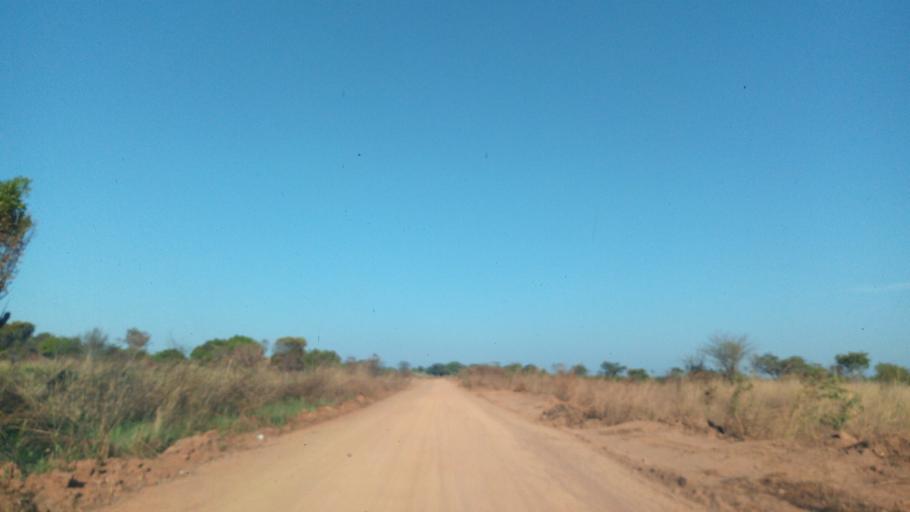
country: ZM
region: Luapula
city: Mwense
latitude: -10.4538
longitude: 28.5473
